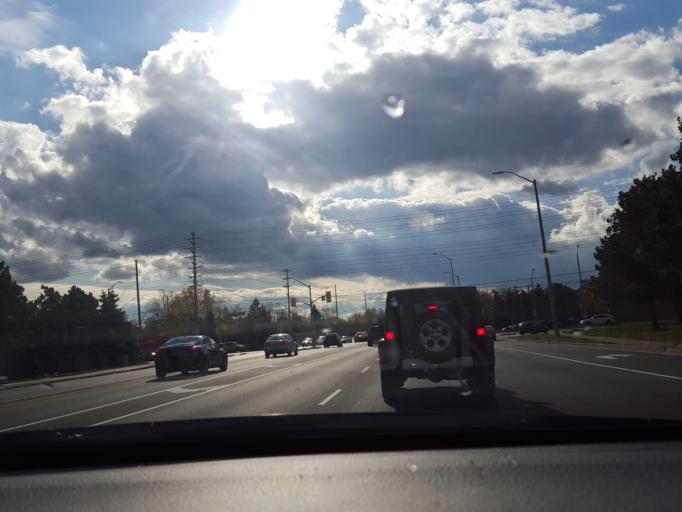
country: CA
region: Ontario
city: Brampton
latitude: 43.5889
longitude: -79.7704
